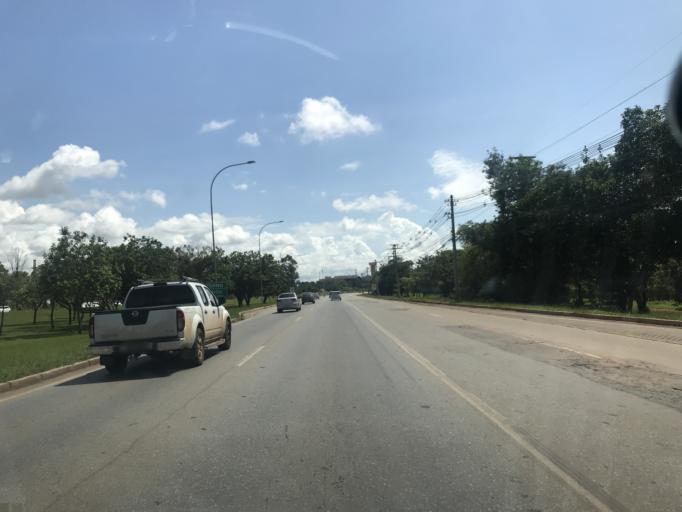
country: BR
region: Federal District
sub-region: Brasilia
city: Brasilia
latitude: -15.8760
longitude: -48.0479
